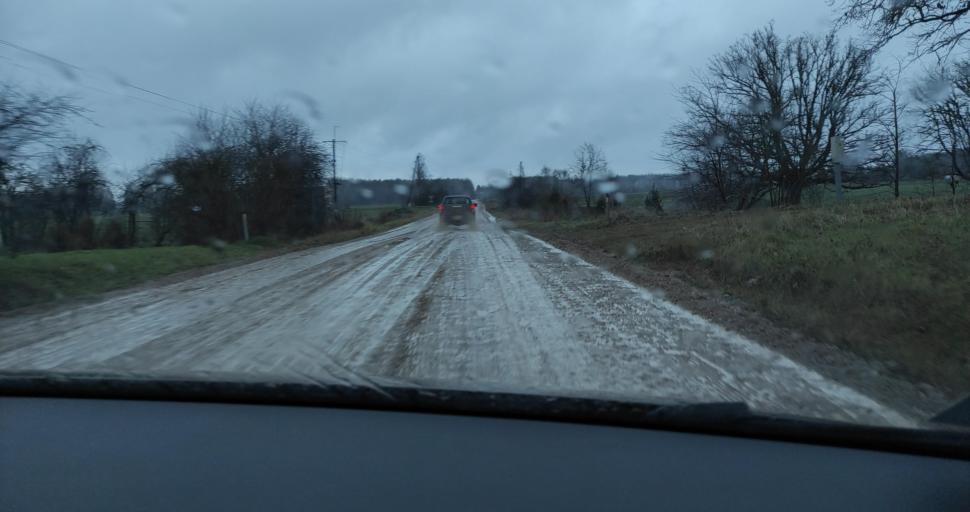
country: LV
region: Skrunda
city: Skrunda
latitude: 56.6780
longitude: 22.2203
